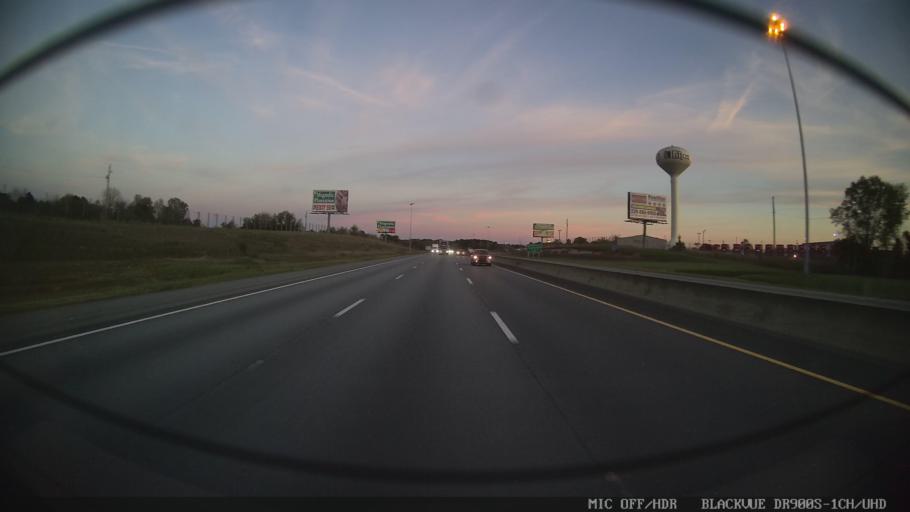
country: US
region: Georgia
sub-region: Tift County
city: Unionville
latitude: 31.4264
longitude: -83.5113
